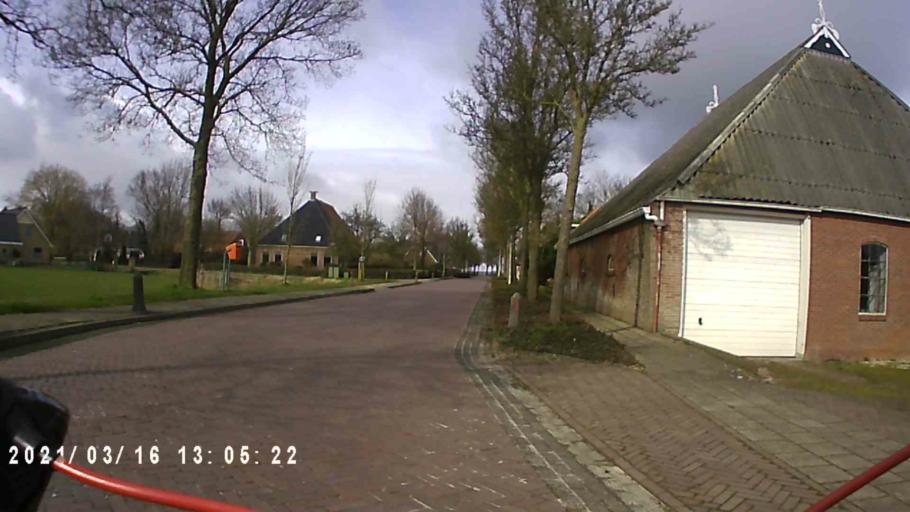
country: NL
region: Friesland
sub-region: Menameradiel
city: Berltsum
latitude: 53.2520
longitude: 5.6276
